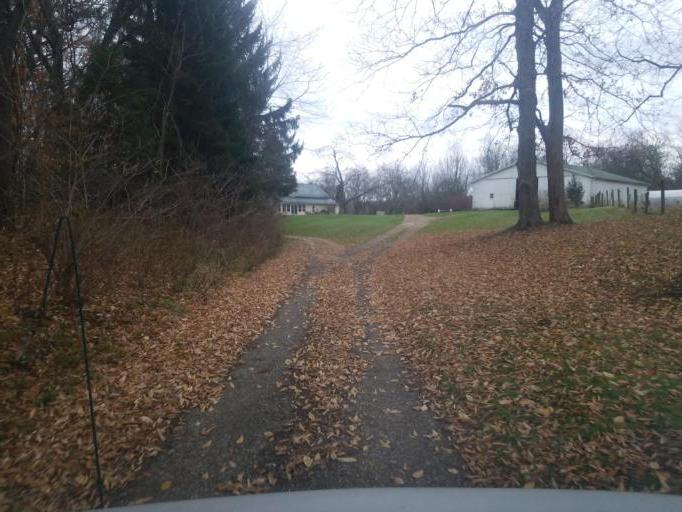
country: US
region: Ohio
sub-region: Knox County
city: Fredericktown
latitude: 40.4495
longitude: -82.5238
